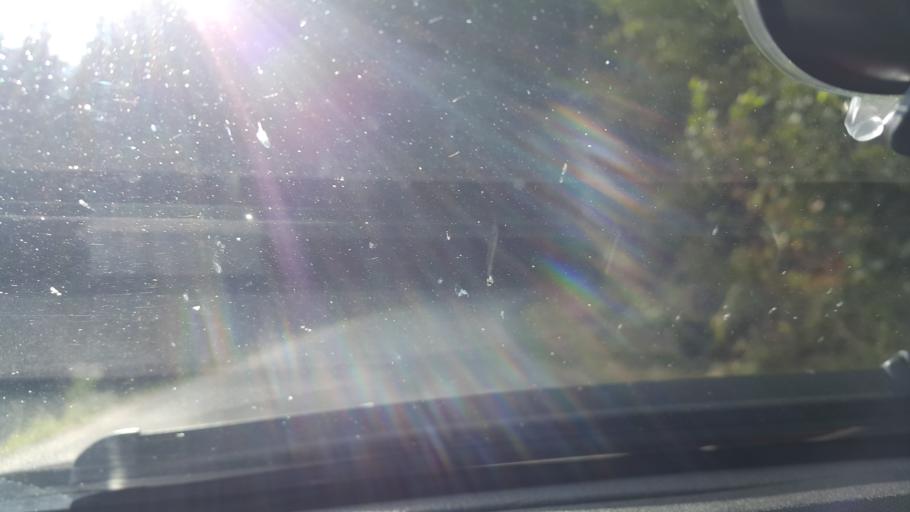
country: AT
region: Styria
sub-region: Politischer Bezirk Deutschlandsberg
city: Wies
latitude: 46.7188
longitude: 15.3046
